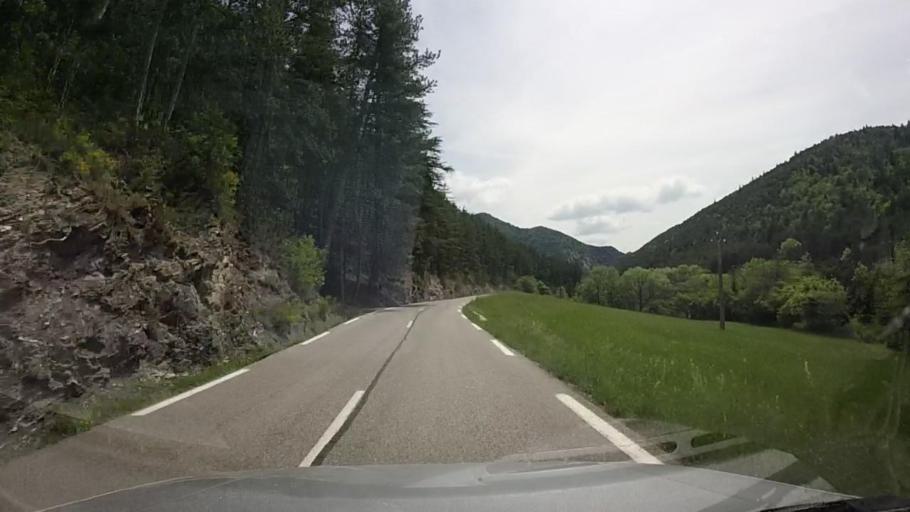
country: FR
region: Provence-Alpes-Cote d'Azur
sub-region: Departement des Alpes-de-Haute-Provence
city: Le Brusquet
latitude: 44.2096
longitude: 6.3681
